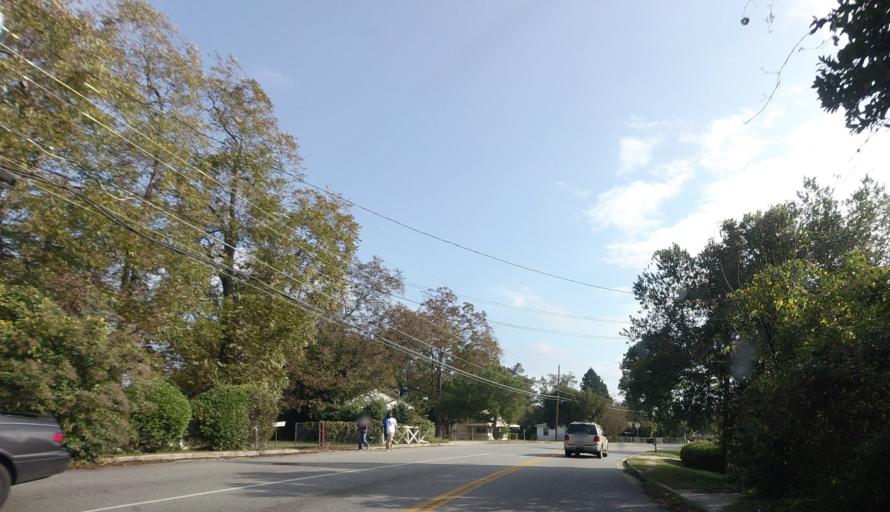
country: US
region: Georgia
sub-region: Bibb County
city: Macon
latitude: 32.8059
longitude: -83.6653
